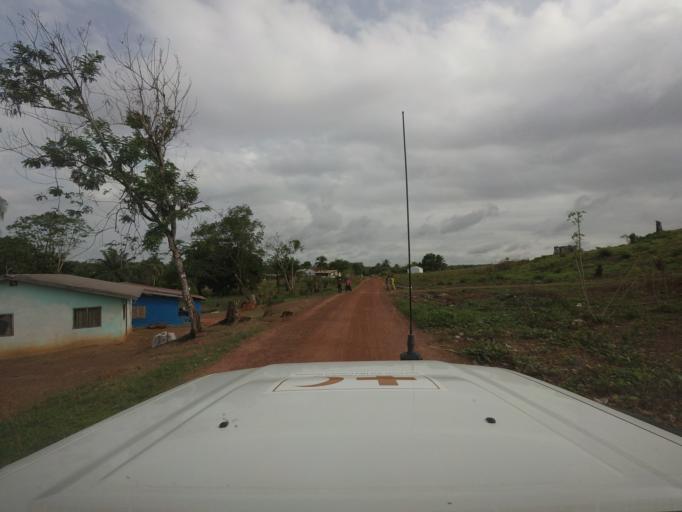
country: LR
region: Bong
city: Gbarnga
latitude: 7.0057
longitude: -9.4745
